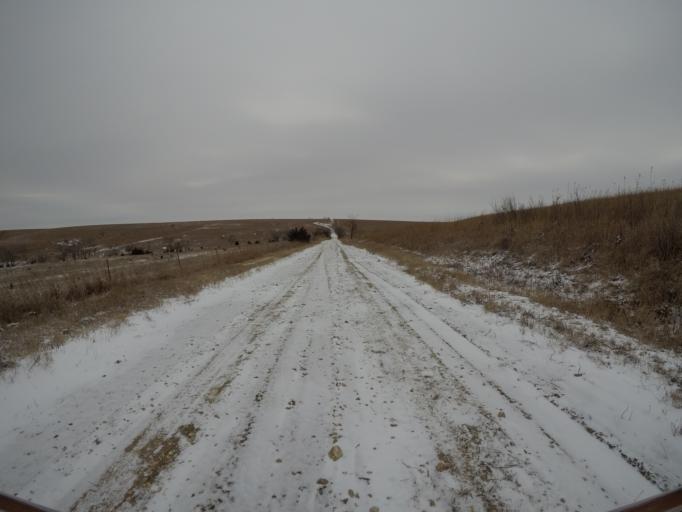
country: US
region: Kansas
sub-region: Wabaunsee County
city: Alma
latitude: 38.8852
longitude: -96.1136
